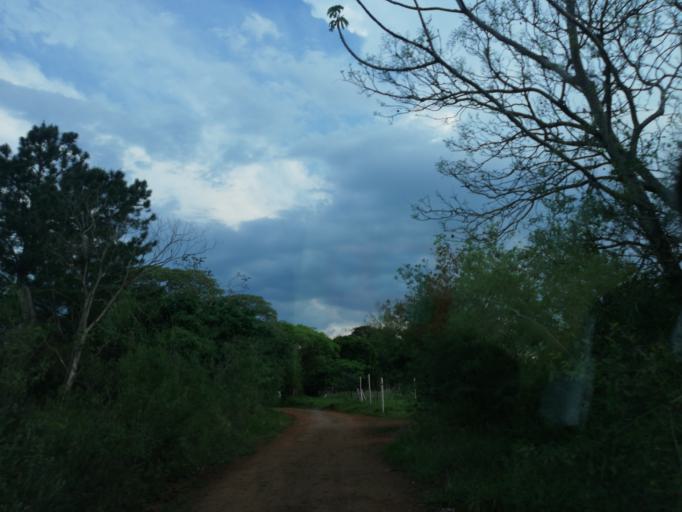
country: AR
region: Misiones
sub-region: Departamento de Capital
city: Posadas
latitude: -27.4015
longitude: -55.9732
